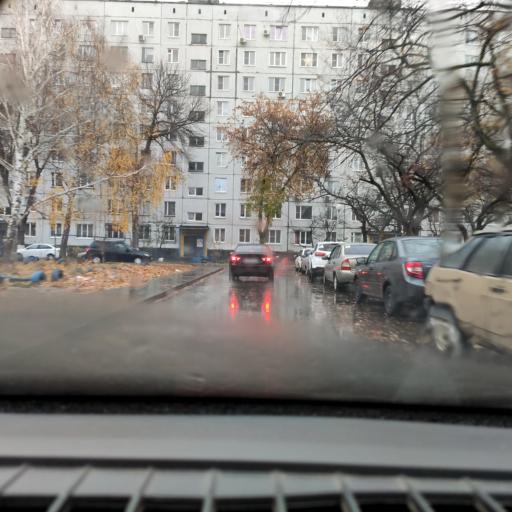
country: RU
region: Samara
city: Tol'yatti
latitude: 53.5319
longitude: 49.2747
